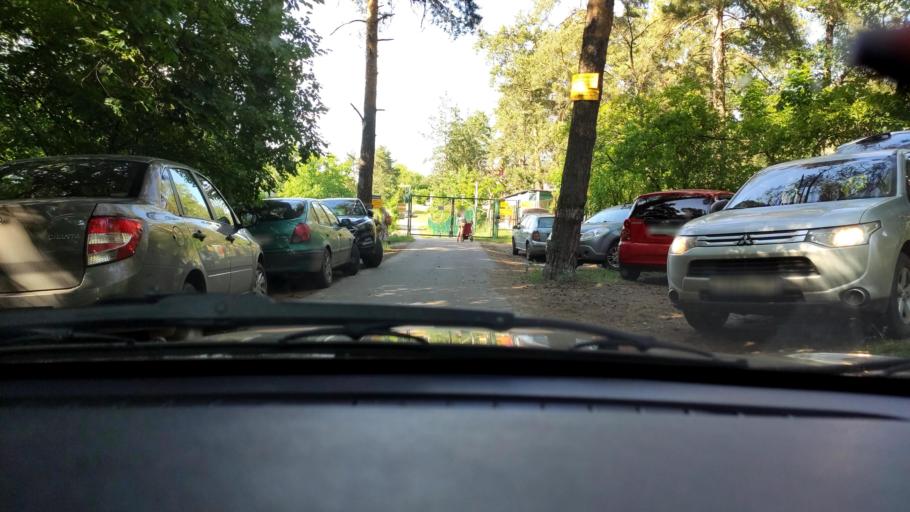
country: RU
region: Voronezj
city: Somovo
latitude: 51.8106
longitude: 39.3844
